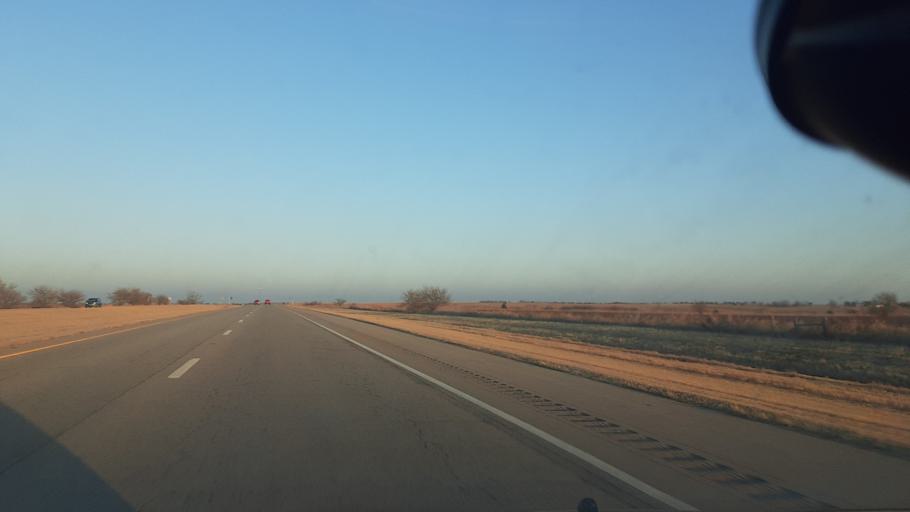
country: US
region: Oklahoma
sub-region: Noble County
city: Perry
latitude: 36.3980
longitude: -97.3755
